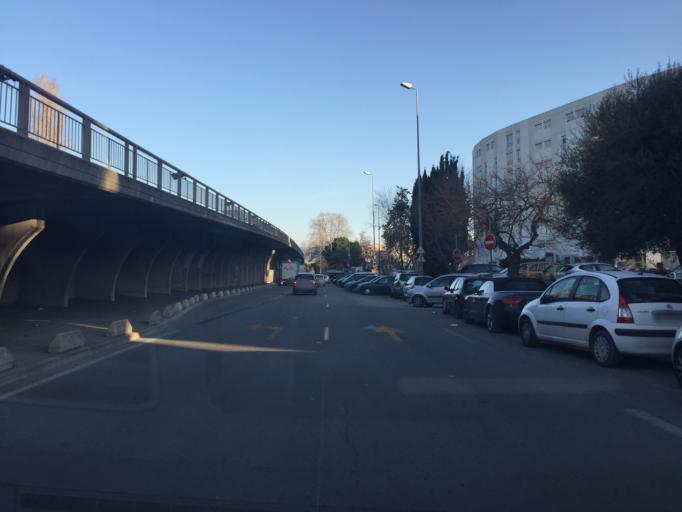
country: FR
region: Provence-Alpes-Cote d'Azur
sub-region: Departement des Alpes-Maritimes
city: Saint-Laurent-du-Var
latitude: 43.6756
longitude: 7.2016
